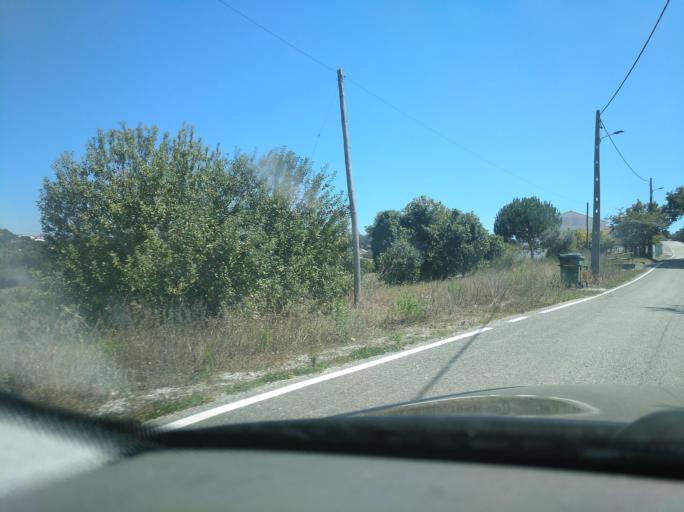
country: PT
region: Leiria
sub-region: Alcobaca
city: Aljubarrota
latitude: 39.5710
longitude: -8.9359
